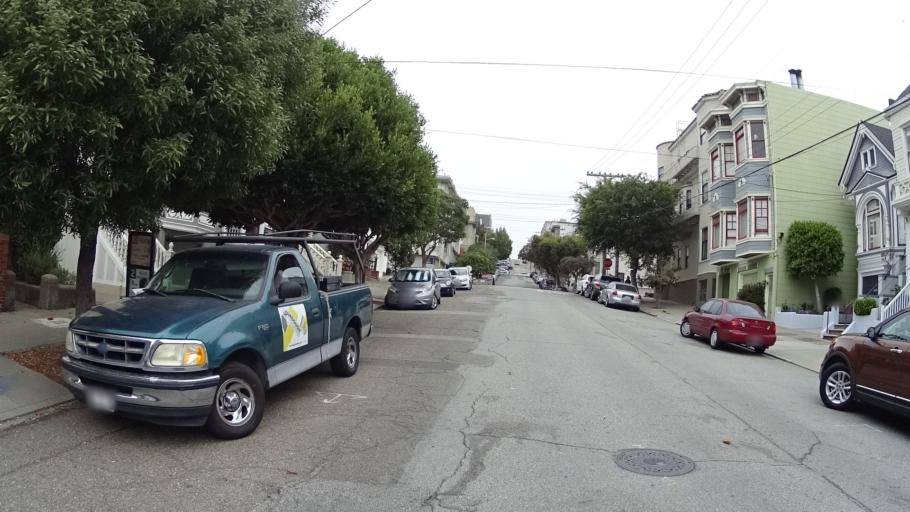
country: US
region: California
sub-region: San Francisco County
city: San Francisco
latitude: 37.7899
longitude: -122.4442
